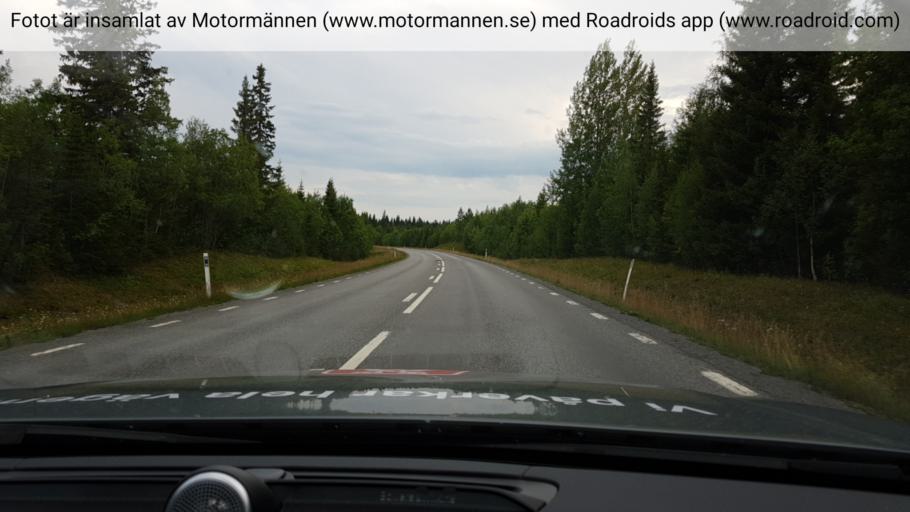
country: SE
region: Jaemtland
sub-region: OEstersunds Kommun
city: Lit
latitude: 63.4700
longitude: 15.1919
